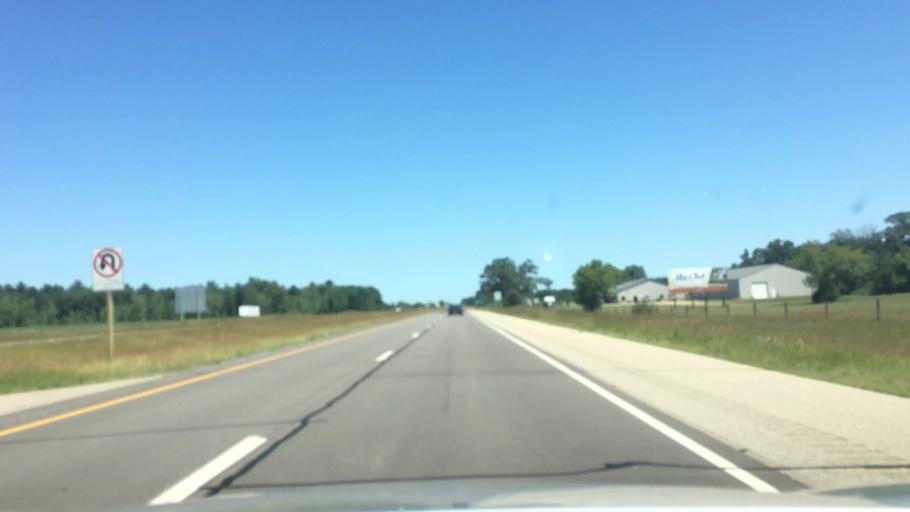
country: US
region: Wisconsin
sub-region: Portage County
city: Plover
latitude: 44.2223
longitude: -89.5243
